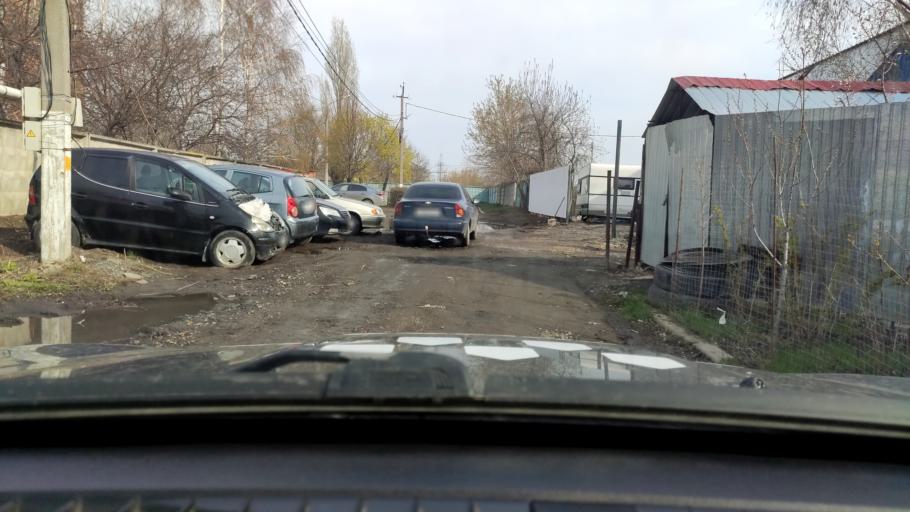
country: RU
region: Samara
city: Tol'yatti
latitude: 53.5413
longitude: 49.4266
